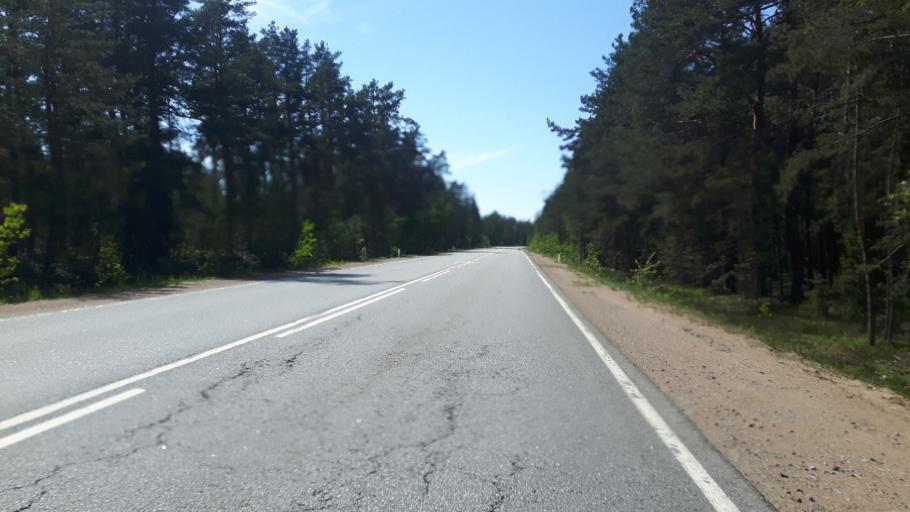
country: RU
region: Leningrad
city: Sista-Palkino
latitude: 59.7677
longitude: 28.8081
